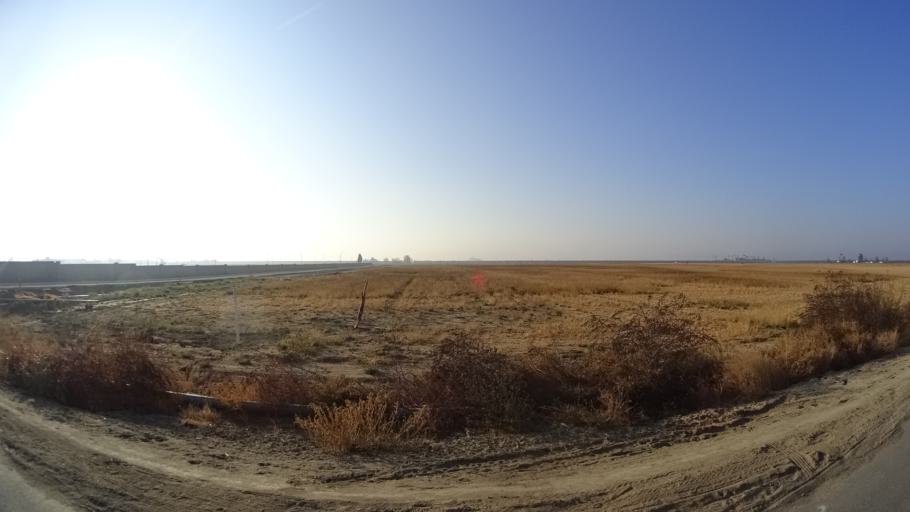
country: US
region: California
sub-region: Kern County
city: Greenacres
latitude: 35.2890
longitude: -119.1192
